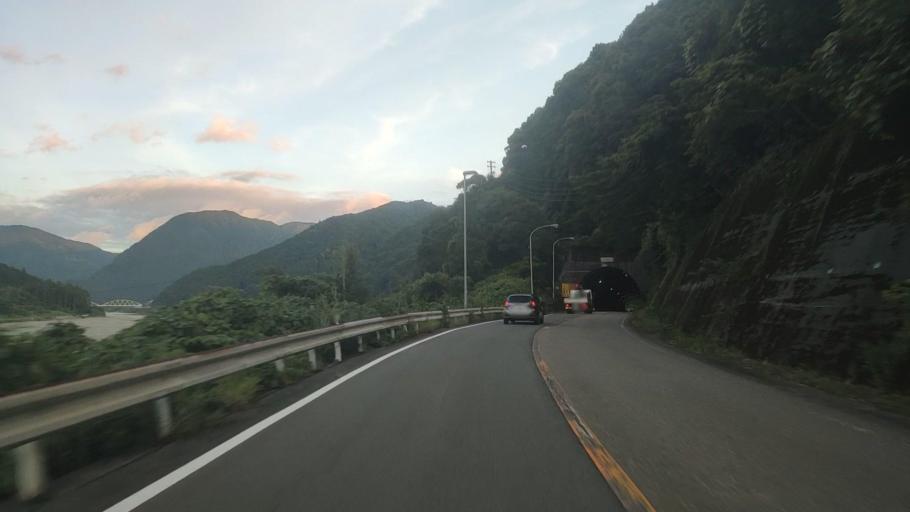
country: JP
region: Wakayama
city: Shingu
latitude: 33.8176
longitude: 135.8562
